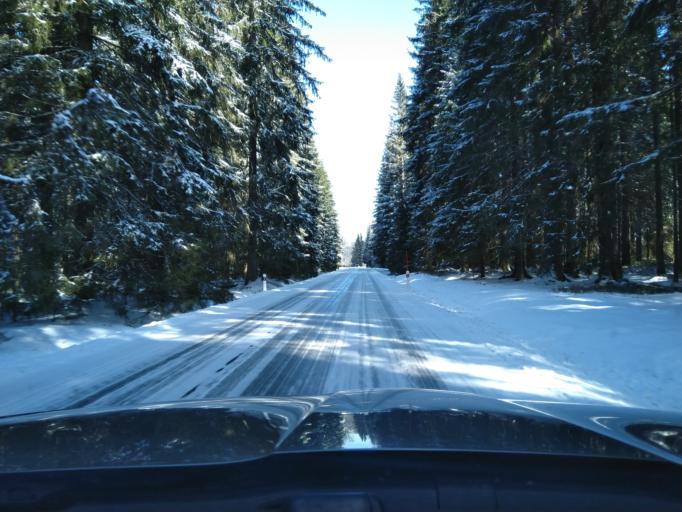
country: CZ
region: Jihocesky
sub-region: Okres Prachatice
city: Borova Lada
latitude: 49.0403
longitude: 13.5786
